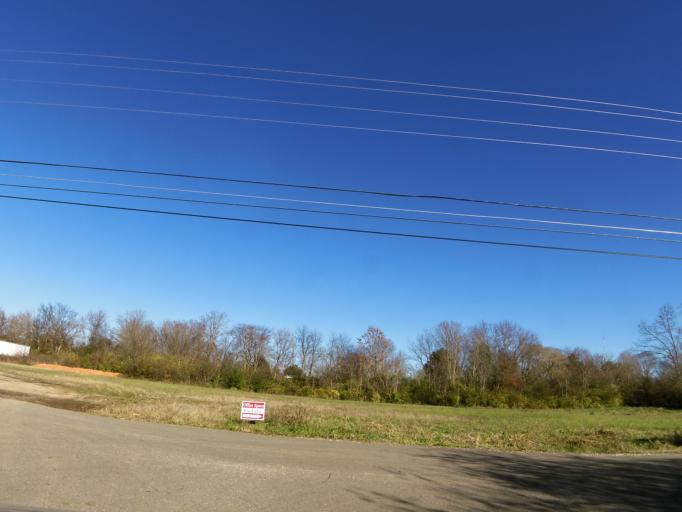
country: US
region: Tennessee
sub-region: Knox County
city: Knoxville
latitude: 36.0080
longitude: -83.9618
